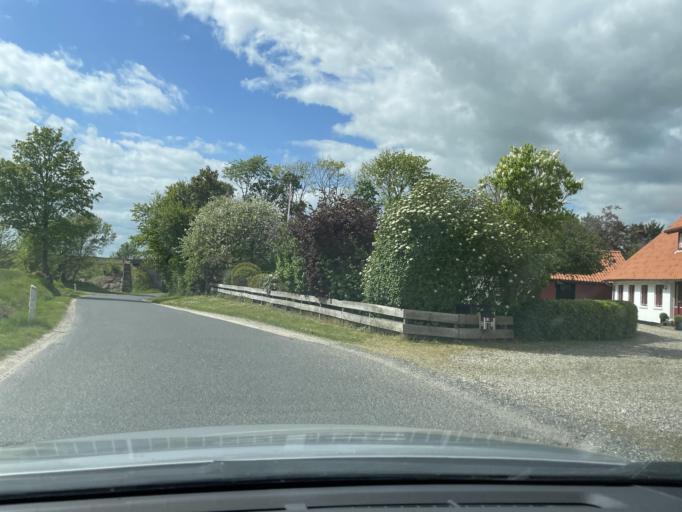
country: DK
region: Central Jutland
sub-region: Skanderborg Kommune
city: Skanderborg
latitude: 55.9272
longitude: 9.9531
